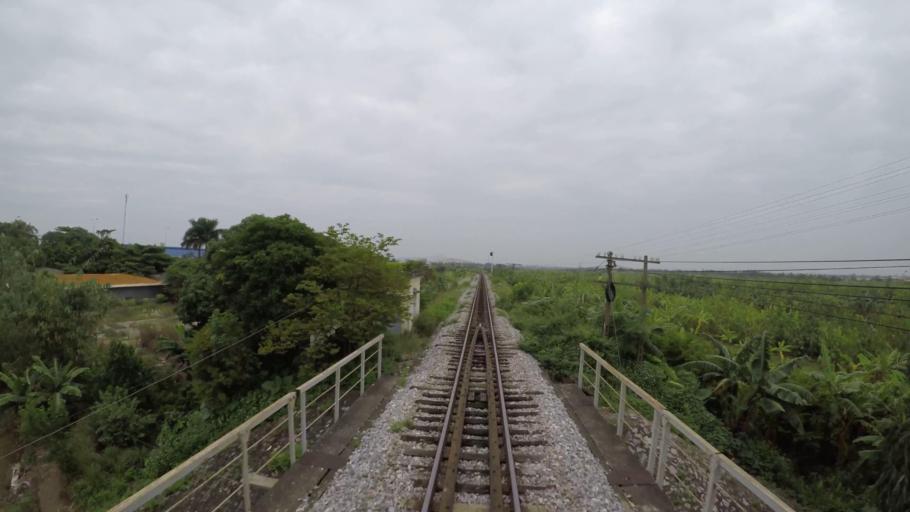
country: VN
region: Hai Duong
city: Nam Sach
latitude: 20.9750
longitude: 106.3931
